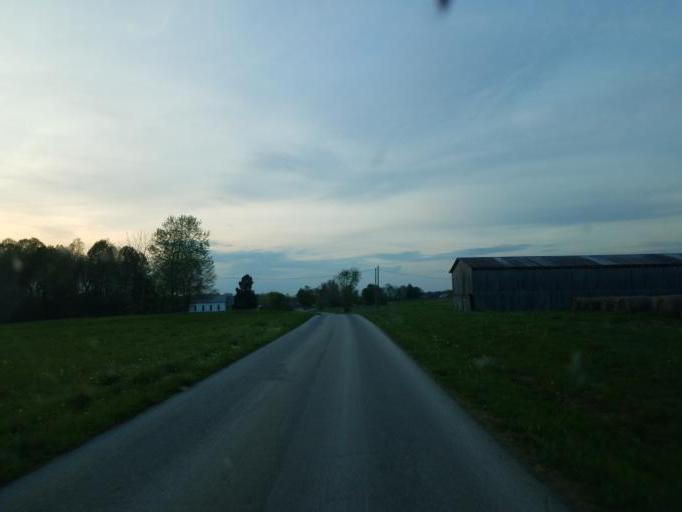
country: US
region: Kentucky
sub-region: Green County
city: Greensburg
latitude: 37.2091
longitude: -85.6951
